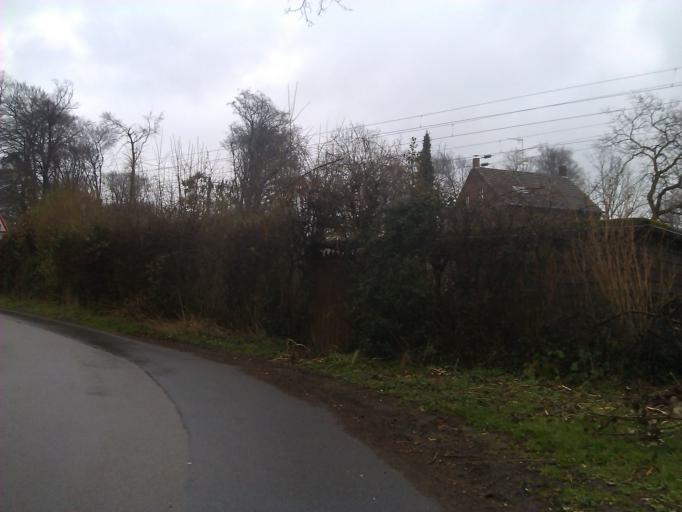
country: DE
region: North Rhine-Westphalia
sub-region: Regierungsbezirk Dusseldorf
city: Ratingen
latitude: 51.3068
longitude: 6.8684
